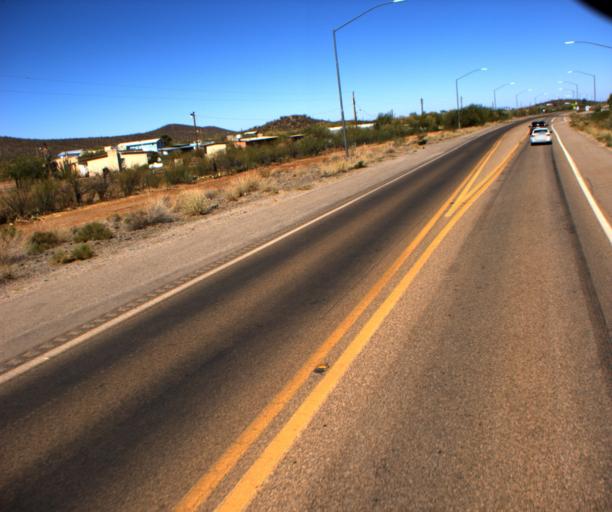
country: US
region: Arizona
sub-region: Pima County
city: Sells
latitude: 31.9159
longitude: -111.8596
